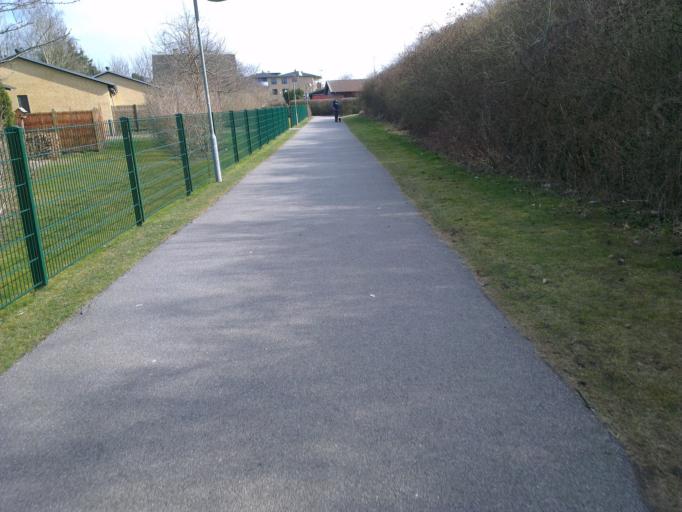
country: DK
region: Capital Region
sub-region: Egedal Kommune
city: Olstykke
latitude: 55.7970
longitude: 12.1560
